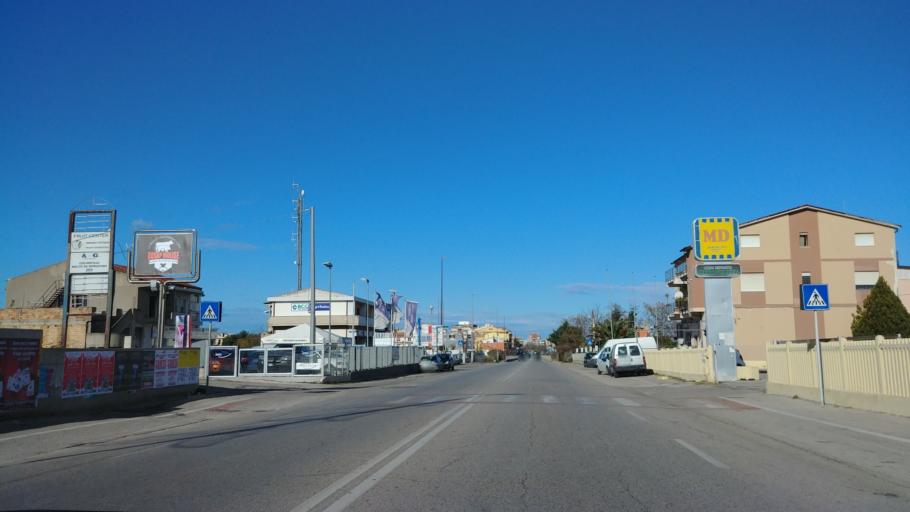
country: IT
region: Molise
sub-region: Provincia di Campobasso
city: Termoli
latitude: 41.9884
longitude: 15.0019
